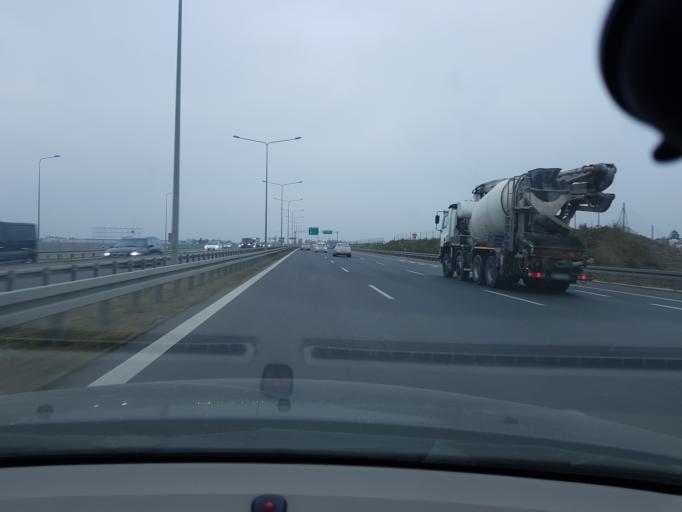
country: PL
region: Masovian Voivodeship
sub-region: Powiat pruszkowski
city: Nowe Grocholice
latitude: 52.1343
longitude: 20.8800
